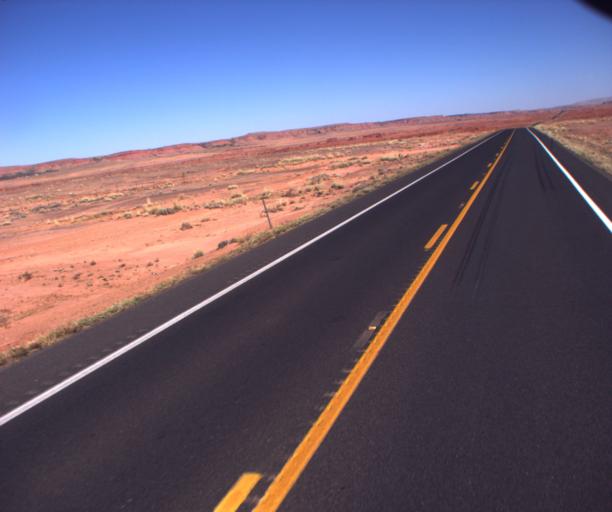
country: US
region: Arizona
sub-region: Coconino County
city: Tuba City
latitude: 36.0972
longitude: -111.3509
